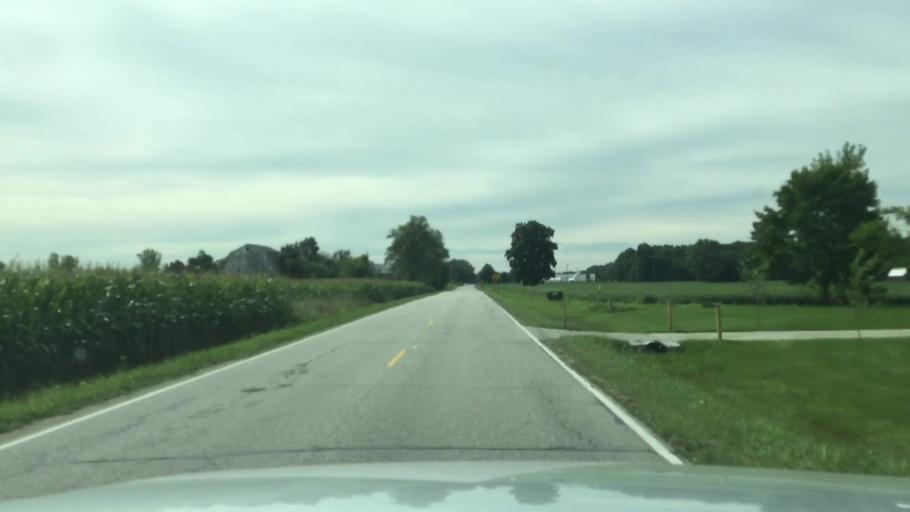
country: US
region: Michigan
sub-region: Genesee County
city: Montrose
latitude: 43.1209
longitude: -83.9880
